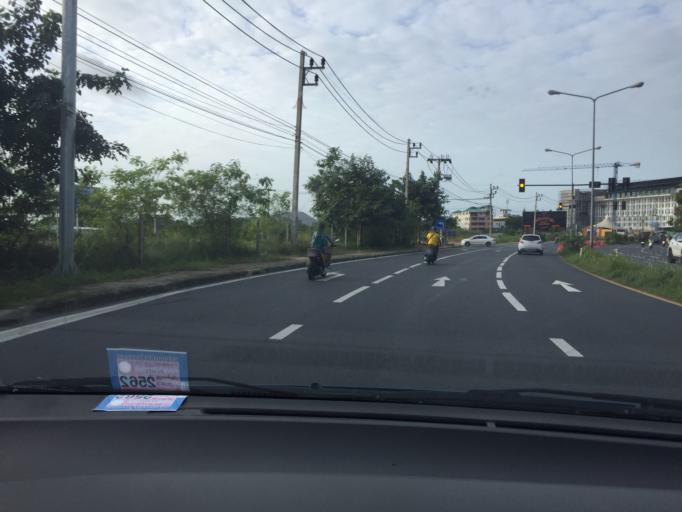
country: TH
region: Phuket
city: Mueang Phuket
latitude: 7.8731
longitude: 98.3568
